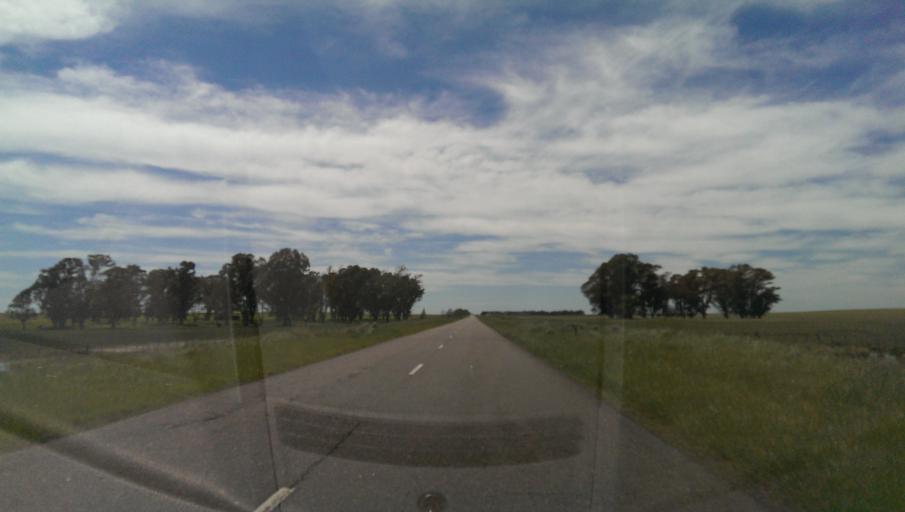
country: AR
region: Buenos Aires
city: Coronel Pringles
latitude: -37.7322
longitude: -61.6209
